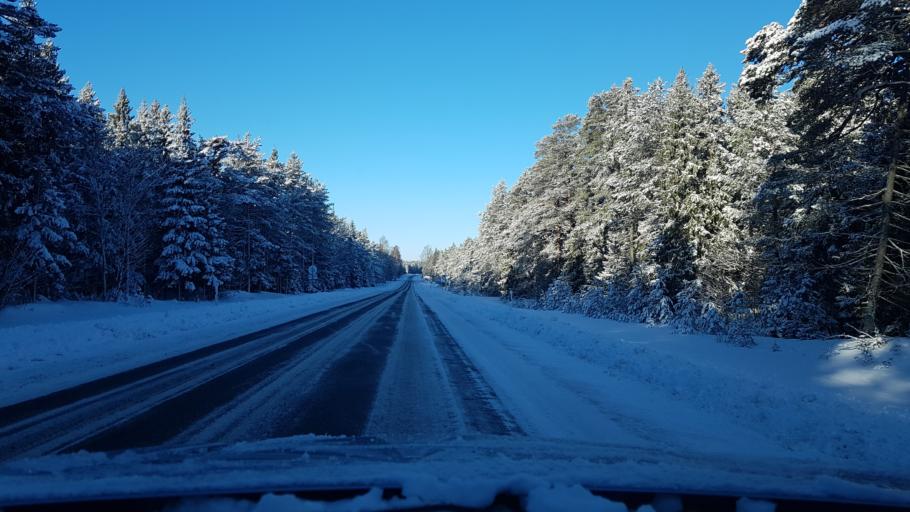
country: EE
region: Hiiumaa
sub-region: Kaerdla linn
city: Kardla
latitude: 58.9608
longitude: 22.8499
